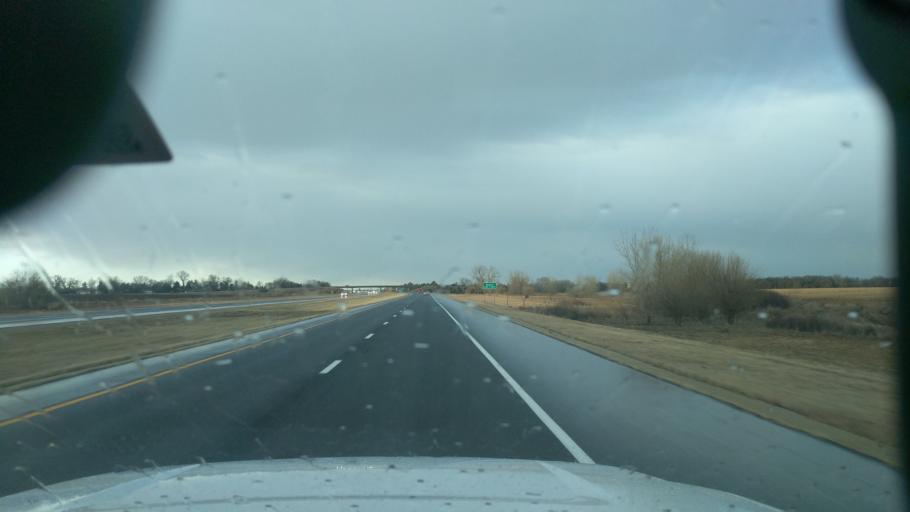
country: US
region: Kansas
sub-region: Harvey County
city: Newton
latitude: 37.9783
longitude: -97.3268
